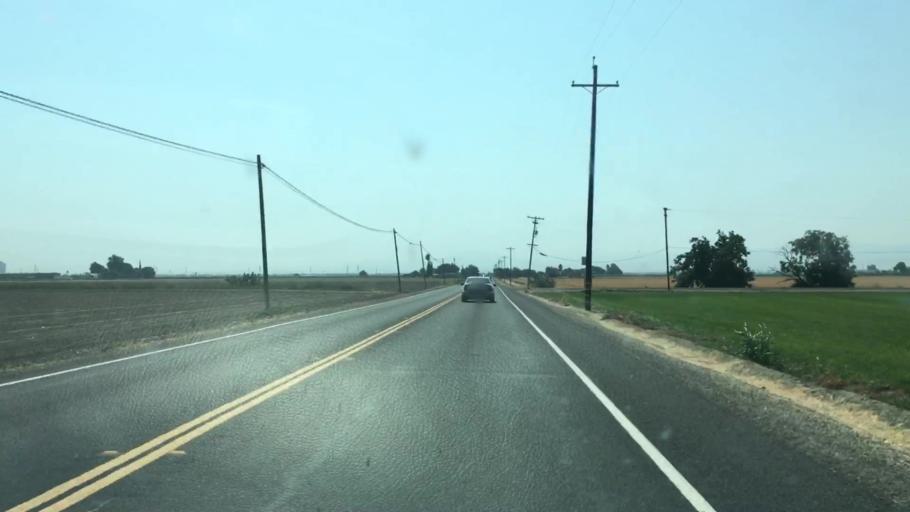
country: US
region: California
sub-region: San Joaquin County
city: Tracy
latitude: 37.7988
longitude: -121.4492
